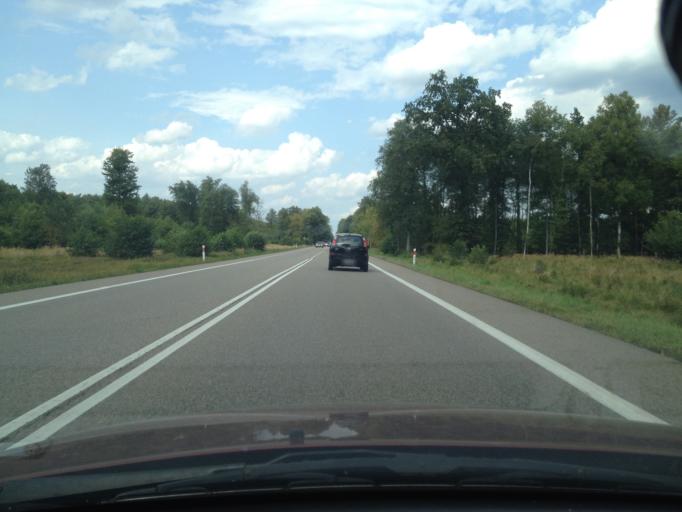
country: PL
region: West Pomeranian Voivodeship
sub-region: Powiat goleniowski
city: Goleniow
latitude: 53.6588
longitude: 14.8153
